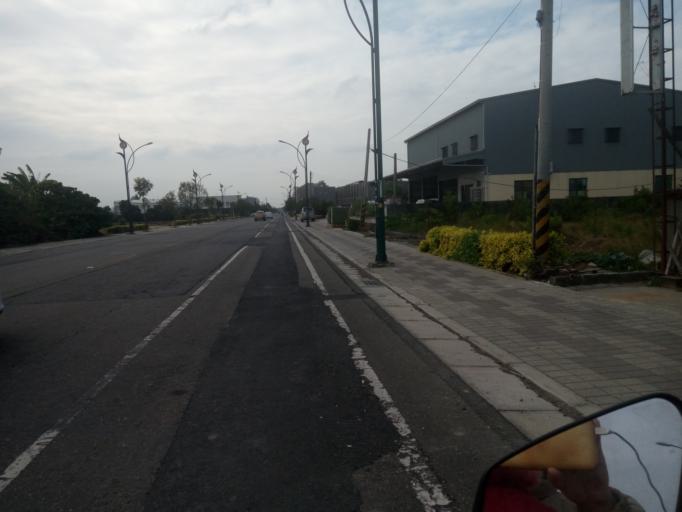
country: TW
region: Taiwan
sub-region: Chiayi
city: Taibao
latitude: 23.4911
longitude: 120.3493
